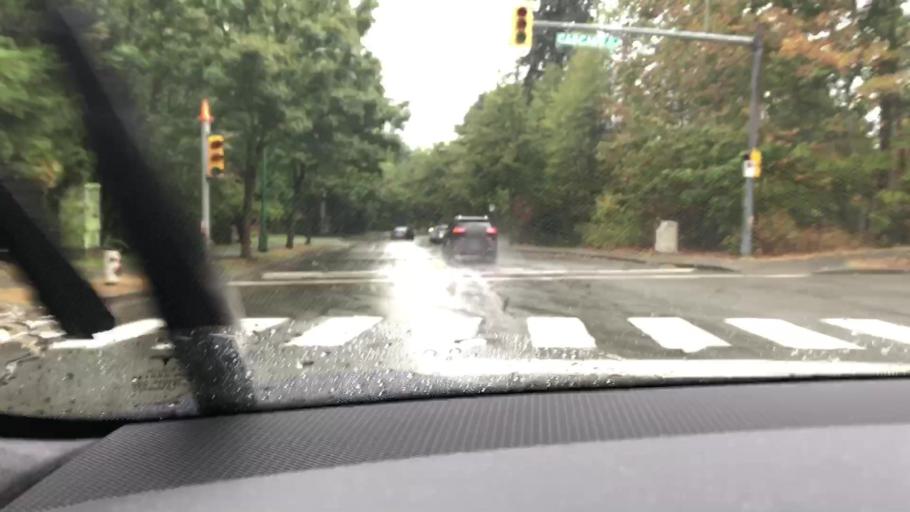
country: CA
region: British Columbia
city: New Westminster
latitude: 49.2361
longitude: -122.9107
